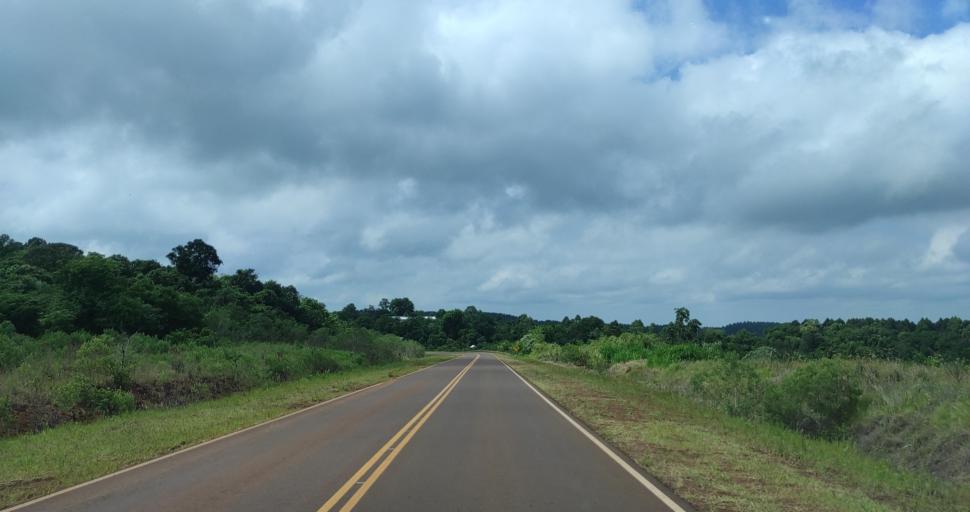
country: AR
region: Misiones
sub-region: Departamento de Veinticinco de Mayo
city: Veinticinco de Mayo
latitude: -27.3700
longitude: -54.8663
